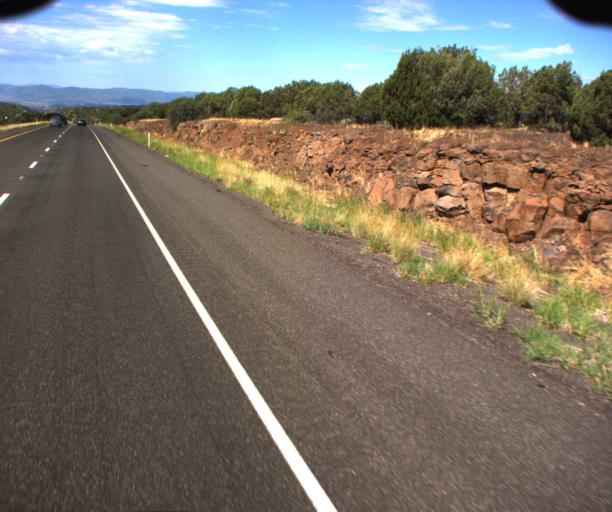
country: US
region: Arizona
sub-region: Yavapai County
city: Big Park
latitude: 34.7321
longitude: -111.7037
